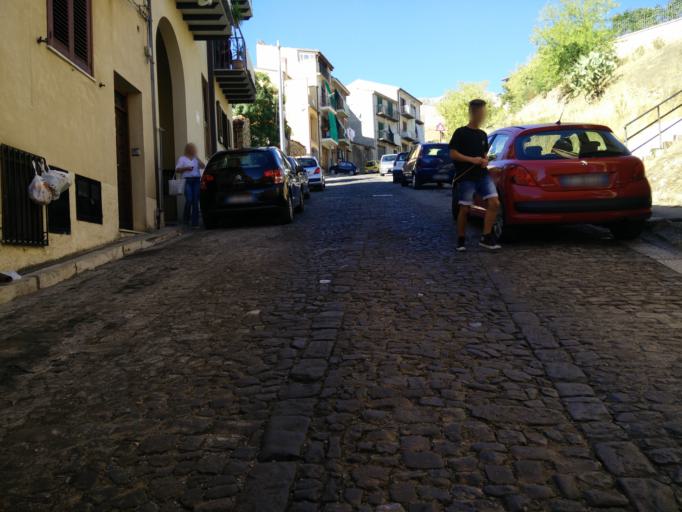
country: IT
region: Sicily
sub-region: Palermo
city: Castelbuono
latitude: 37.9271
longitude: 14.0898
